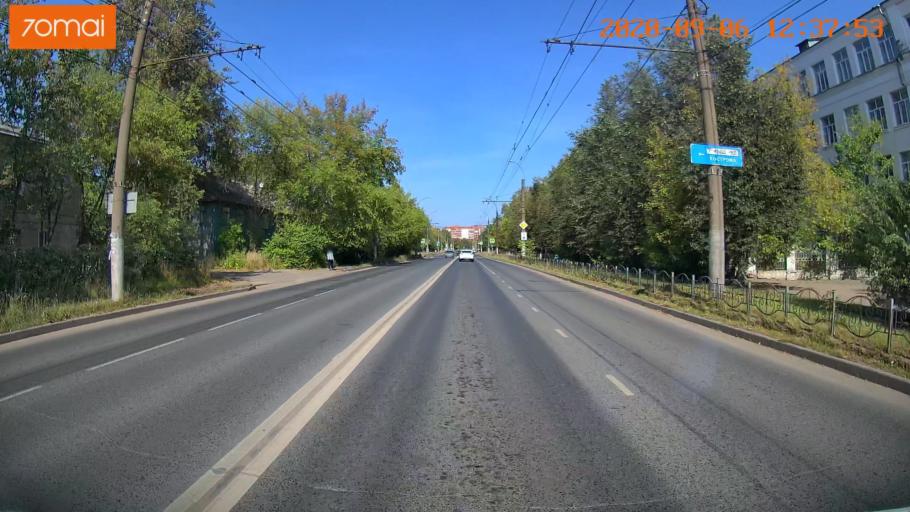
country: RU
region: Ivanovo
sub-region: Gorod Ivanovo
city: Ivanovo
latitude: 57.0291
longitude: 40.9804
